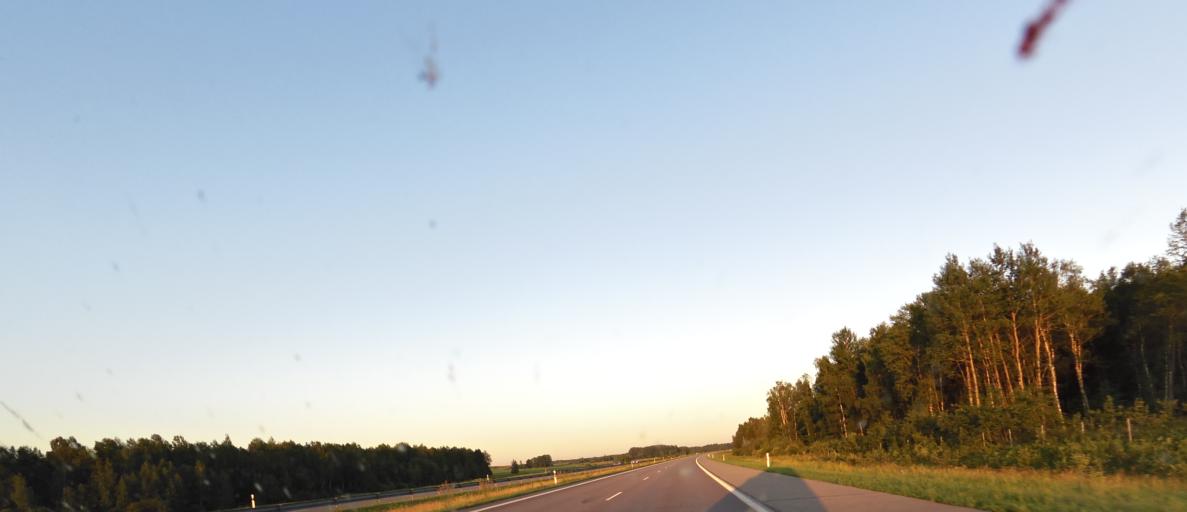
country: LT
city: Sirvintos
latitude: 54.9066
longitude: 25.0252
